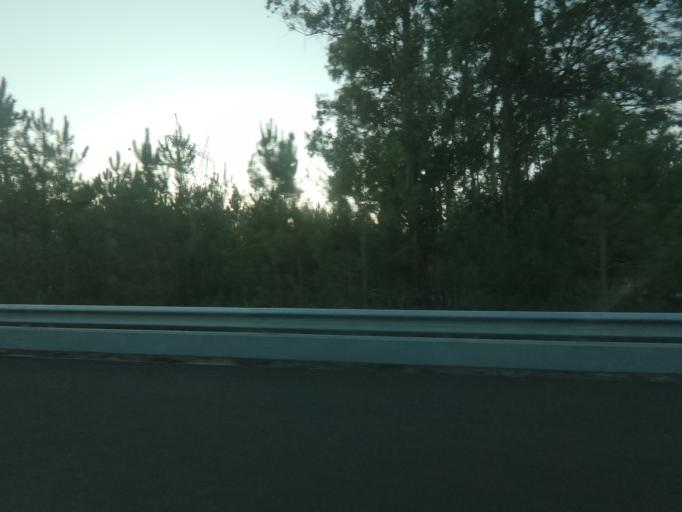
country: PT
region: Leiria
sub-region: Pombal
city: Pombal
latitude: 39.8815
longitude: -8.6969
